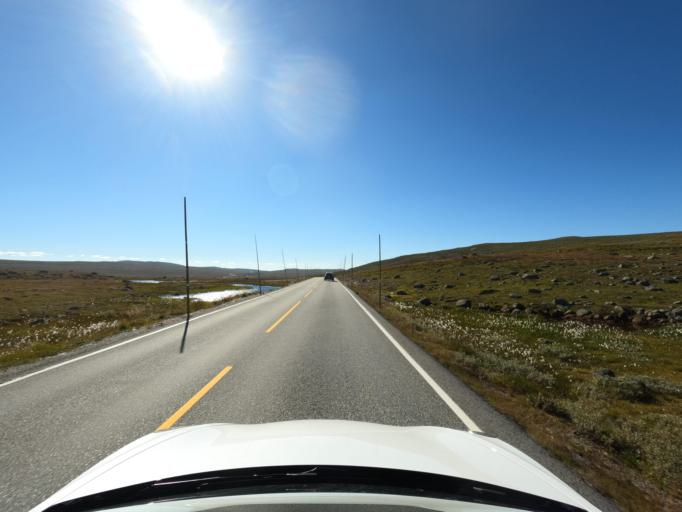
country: NO
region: Hordaland
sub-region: Eidfjord
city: Eidfjord
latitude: 60.4079
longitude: 7.6374
